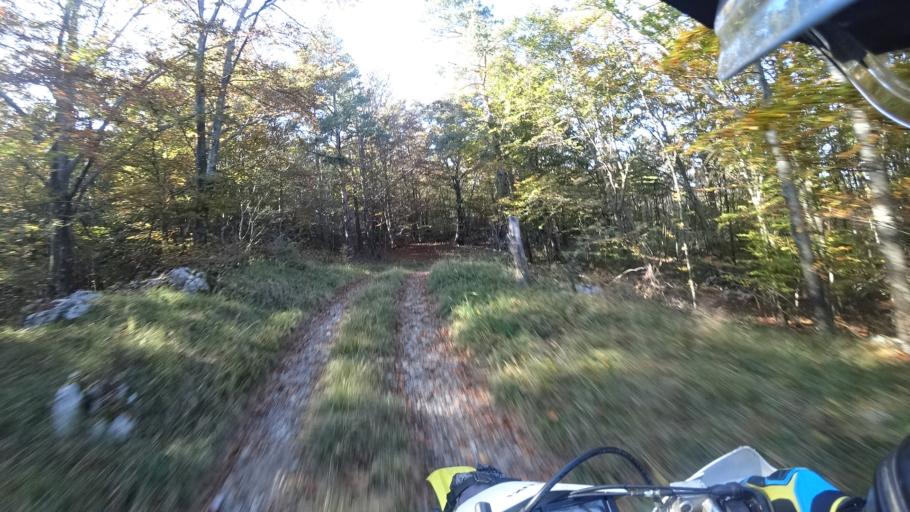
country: HR
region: Primorsko-Goranska
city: Klana
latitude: 45.4586
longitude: 14.3375
